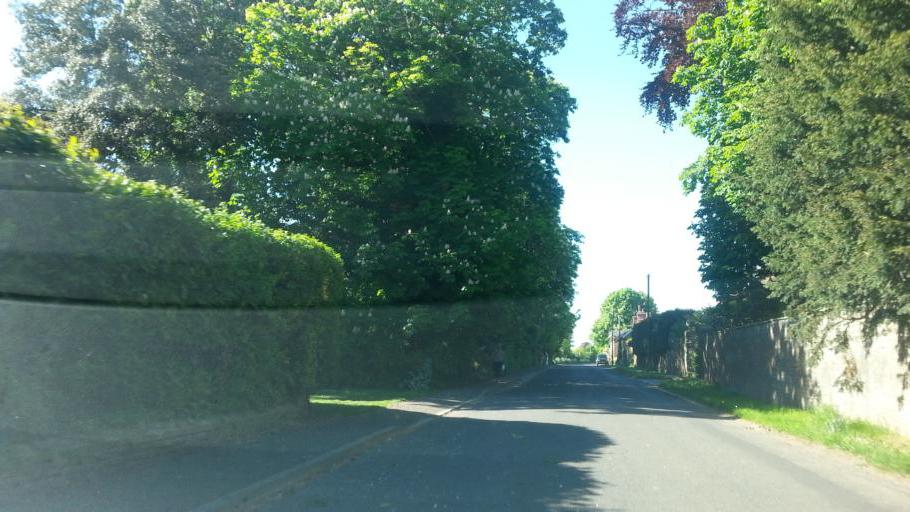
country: GB
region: England
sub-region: Somerset
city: Milborne Port
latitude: 50.9693
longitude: -2.4618
